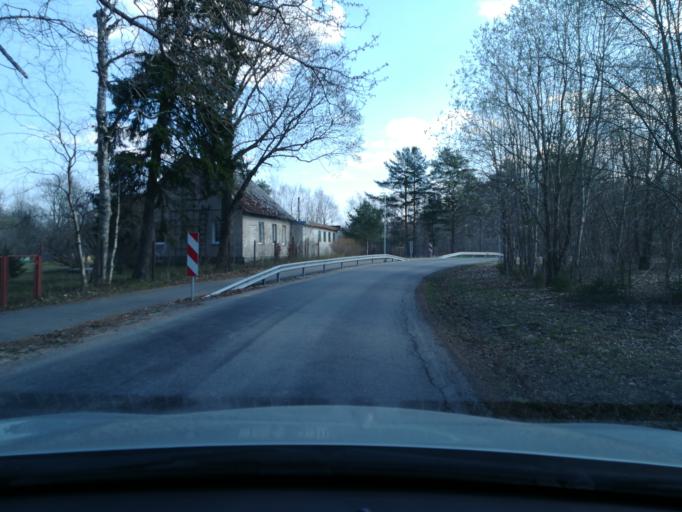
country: EE
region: Harju
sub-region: Saue vald
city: Laagri
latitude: 59.3548
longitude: 24.5768
